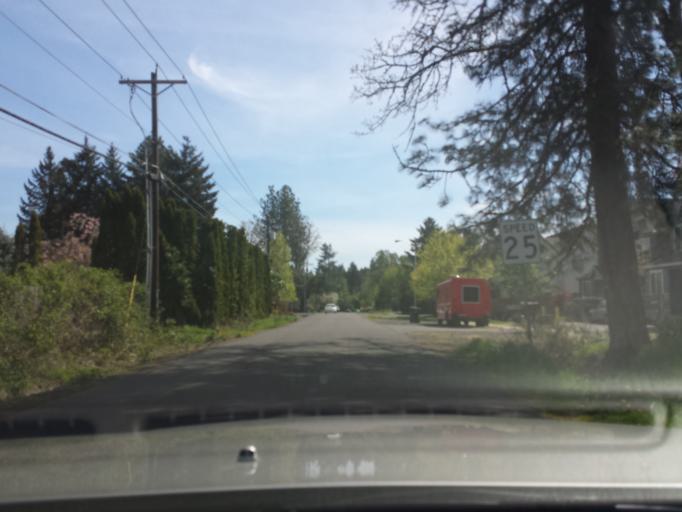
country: US
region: Oregon
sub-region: Washington County
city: Aloha
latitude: 45.4996
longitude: -122.8602
